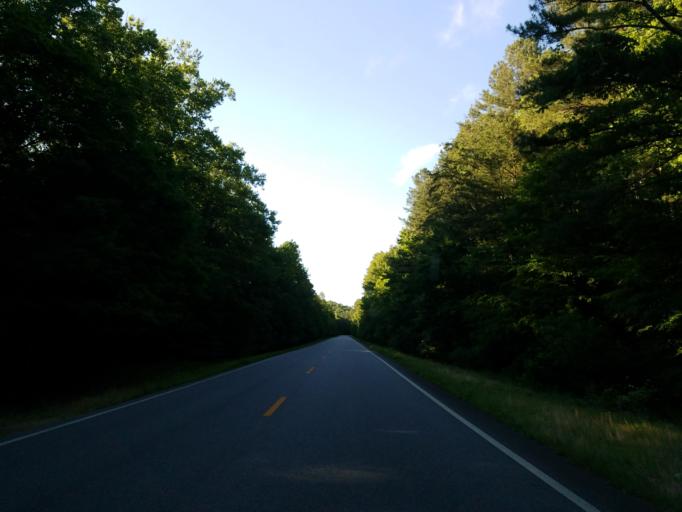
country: US
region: Georgia
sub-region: Whitfield County
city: Dalton
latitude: 34.6474
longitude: -85.0611
